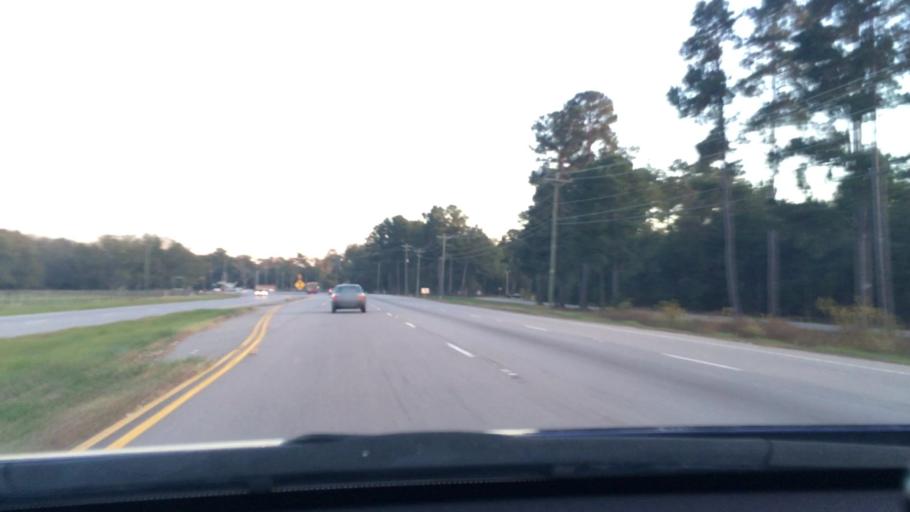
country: US
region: South Carolina
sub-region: Richland County
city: Hopkins
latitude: 33.9430
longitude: -80.8045
